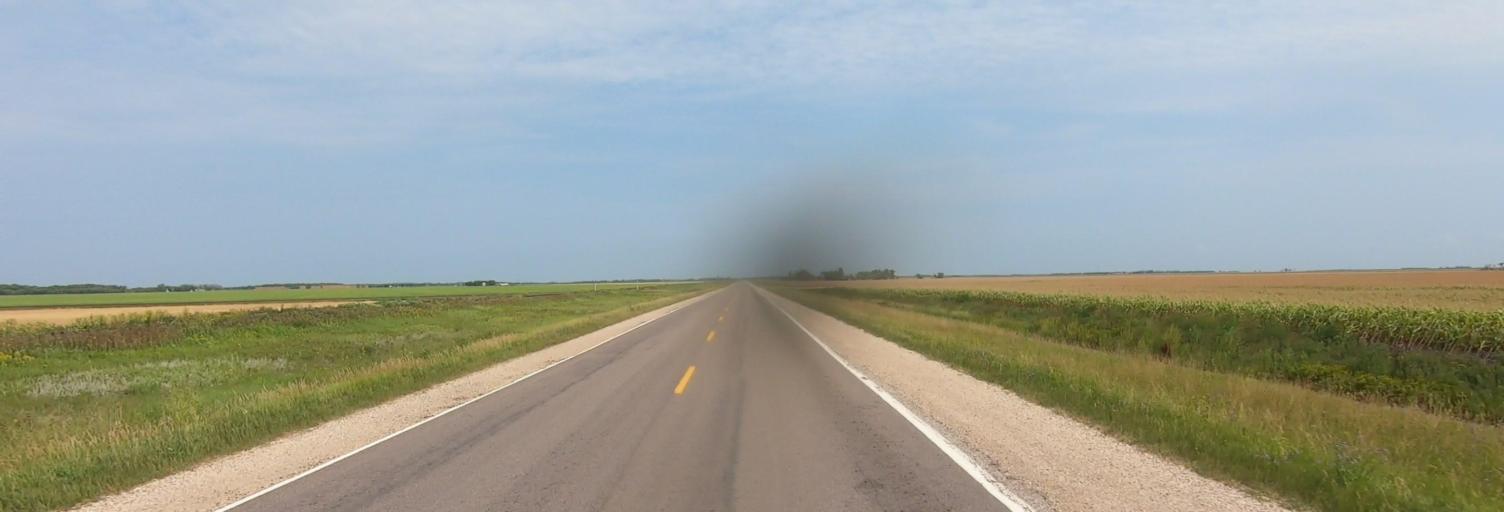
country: CA
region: Manitoba
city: Headingley
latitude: 49.6475
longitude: -97.2974
